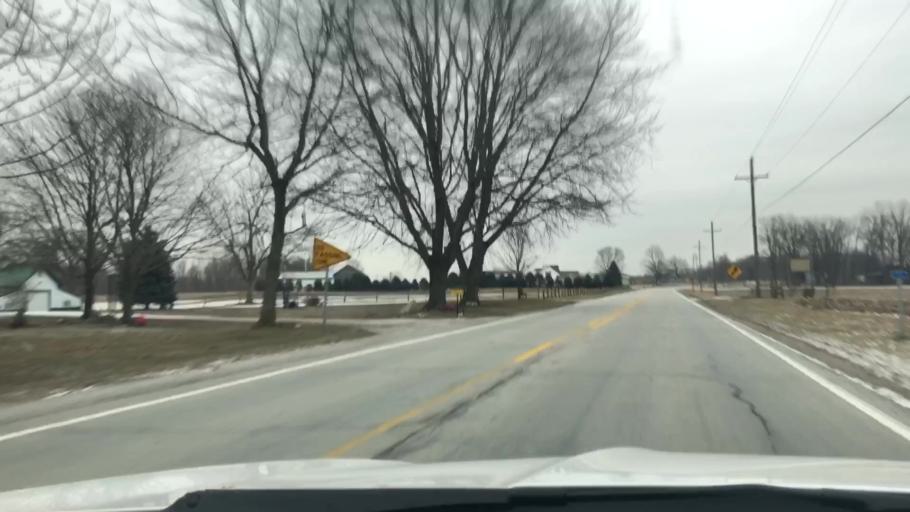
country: US
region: Indiana
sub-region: Fulton County
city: Rochester
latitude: 41.0564
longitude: -86.1623
